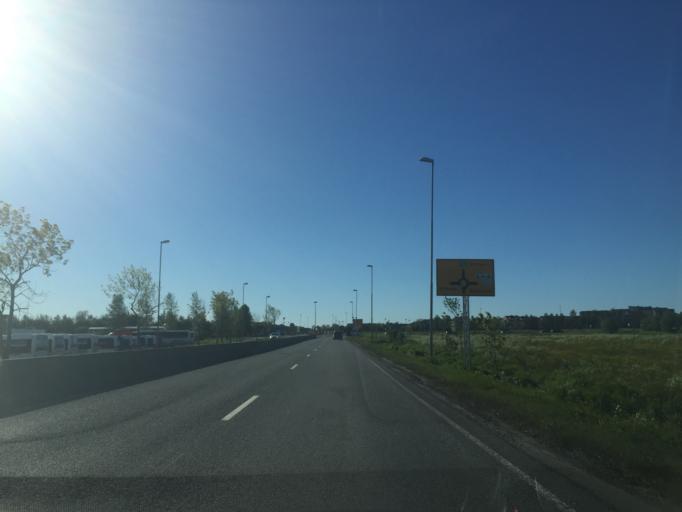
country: NO
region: Nordland
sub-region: Bodo
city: Bodo
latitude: 67.2801
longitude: 14.4253
